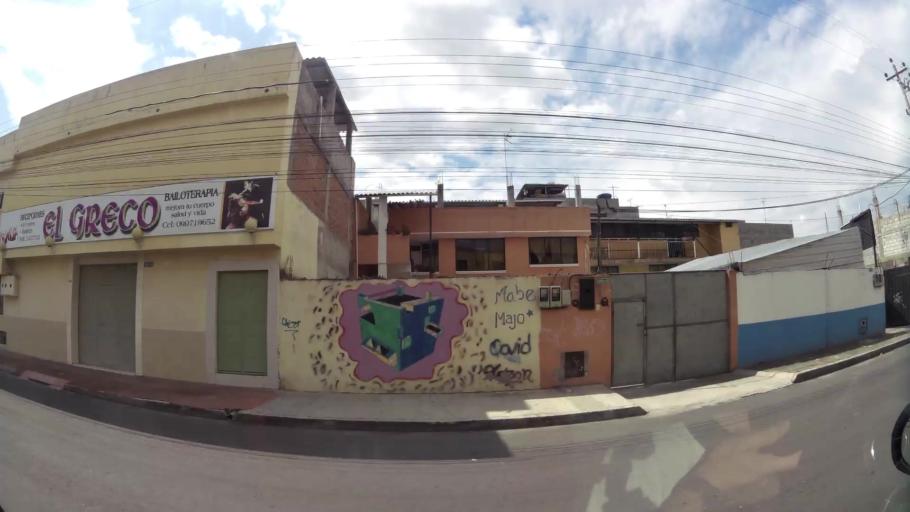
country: EC
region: Pichincha
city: Quito
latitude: -0.1009
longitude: -78.4547
